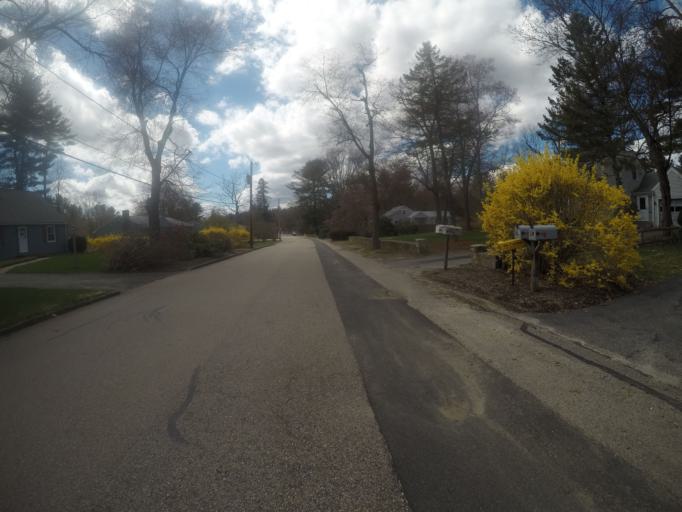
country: US
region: Massachusetts
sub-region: Bristol County
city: Easton
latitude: 42.0308
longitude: -71.0716
